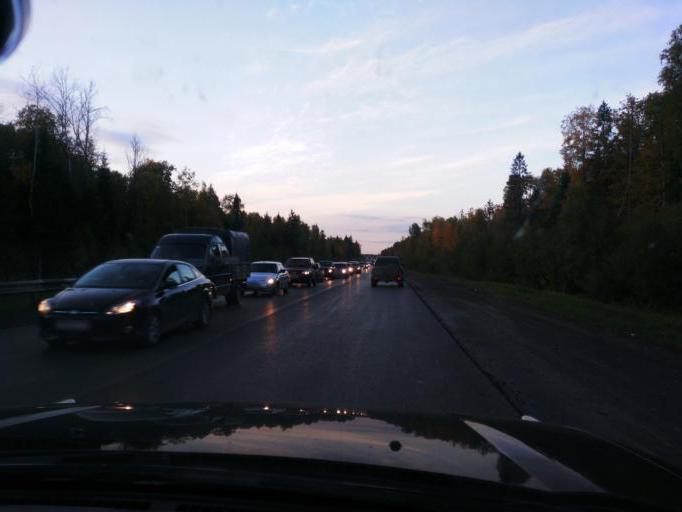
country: RU
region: Perm
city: Novyye Lyady
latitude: 58.0734
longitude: 56.4317
